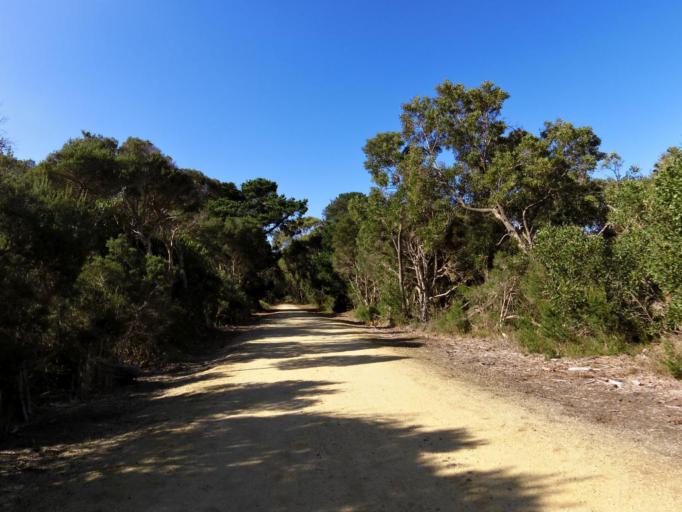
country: AU
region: Victoria
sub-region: Bass Coast
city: North Wonthaggi
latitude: -38.5948
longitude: 145.5647
